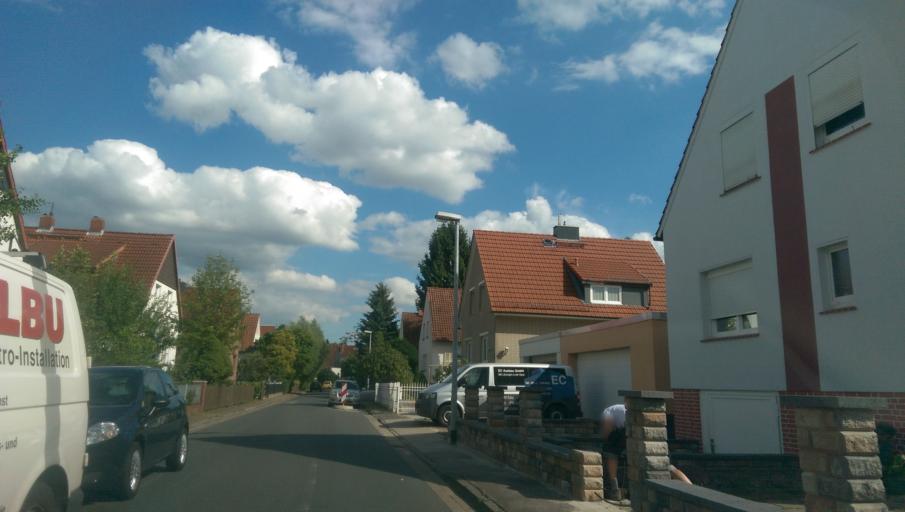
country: DE
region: Lower Saxony
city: Langenhagen
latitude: 52.4147
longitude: 9.7057
